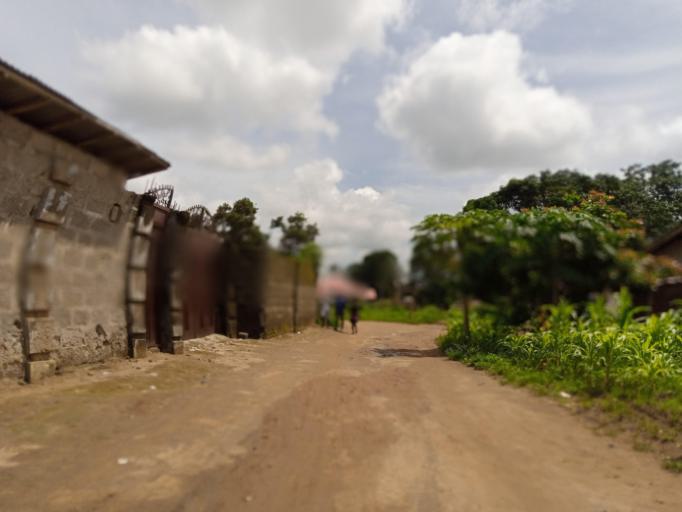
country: SL
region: Northern Province
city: Masoyila
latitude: 8.6034
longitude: -13.1816
